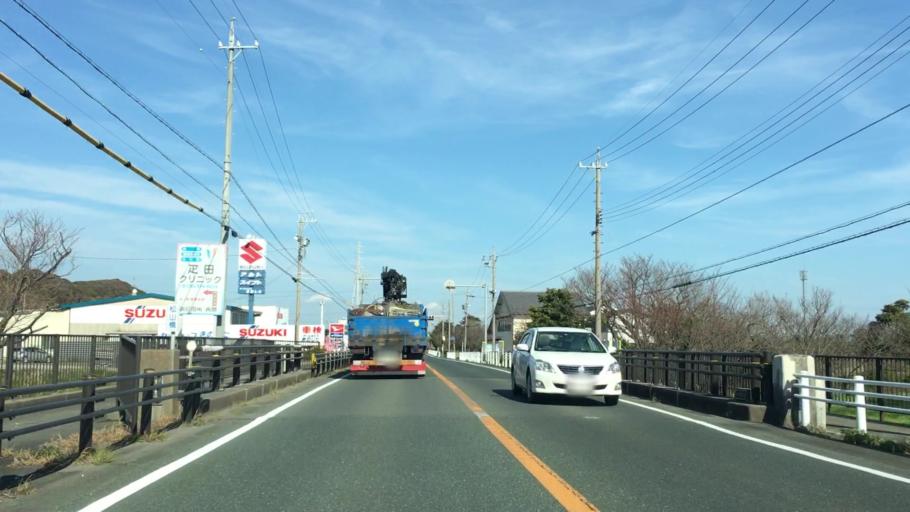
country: JP
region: Shizuoka
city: Kosai-shi
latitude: 34.6844
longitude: 137.5492
